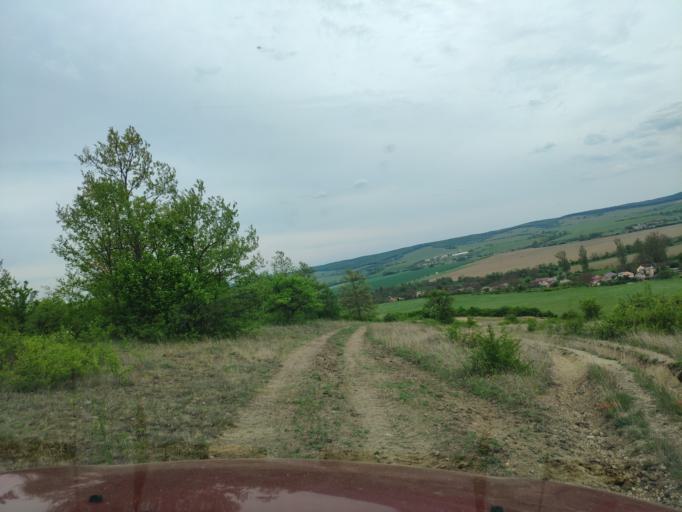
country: HU
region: Borsod-Abauj-Zemplen
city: Putnok
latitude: 48.4894
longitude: 20.3317
